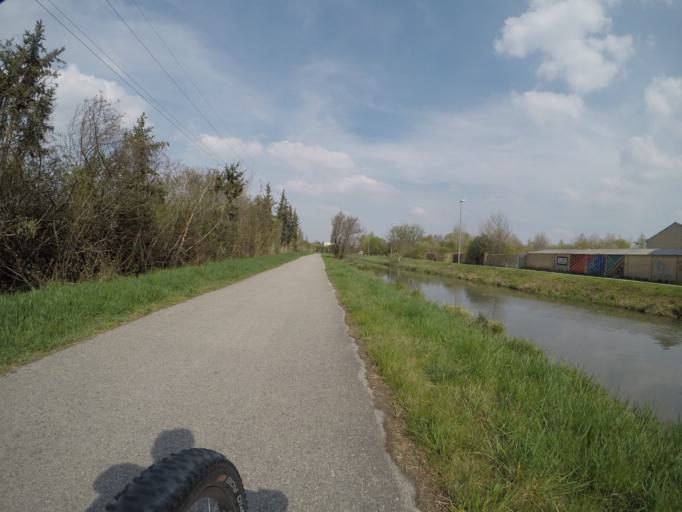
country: AT
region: Lower Austria
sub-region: Politischer Bezirk Modling
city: Guntramsdorf
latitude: 48.0437
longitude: 16.2999
